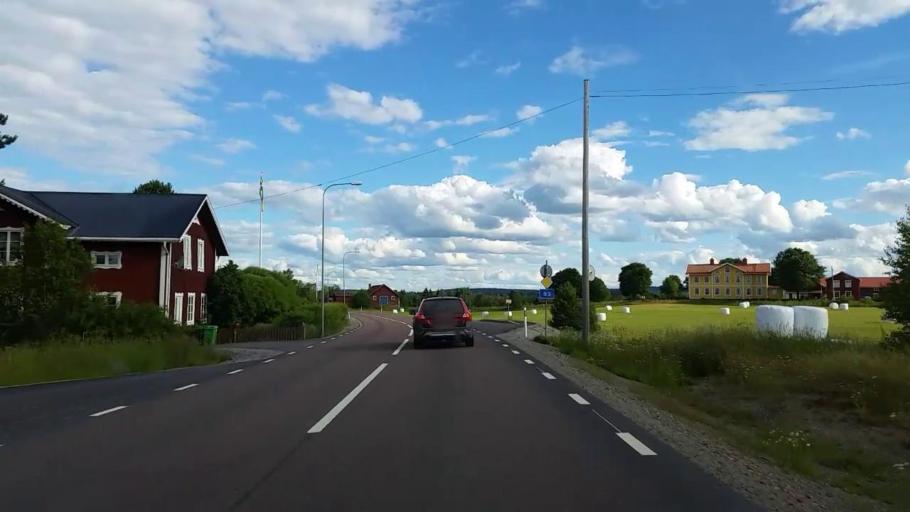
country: SE
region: Gaevleborg
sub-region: Ljusdals Kommun
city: Ljusdal
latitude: 61.8500
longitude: 15.9953
